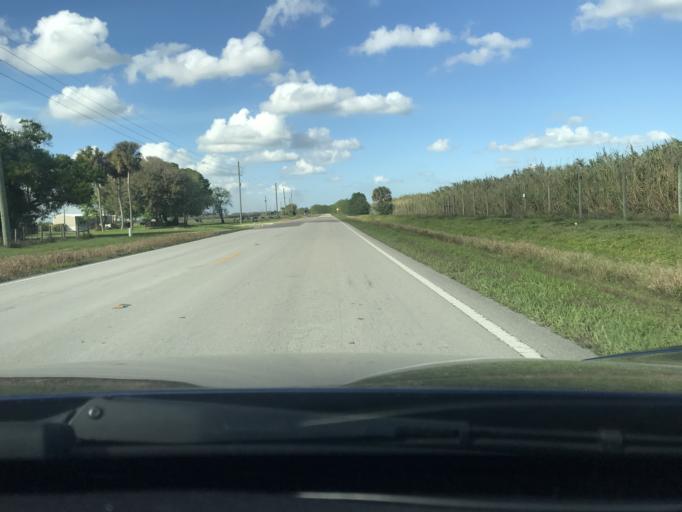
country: US
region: Florida
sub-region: Okeechobee County
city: Taylor Creek
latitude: 27.2707
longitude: -80.6947
